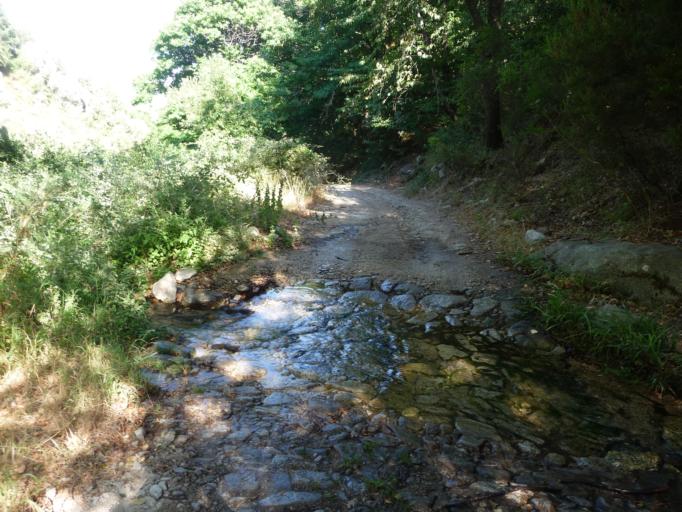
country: IT
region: Calabria
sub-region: Provincia di Reggio Calabria
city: Bivongi
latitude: 38.4878
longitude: 16.4168
